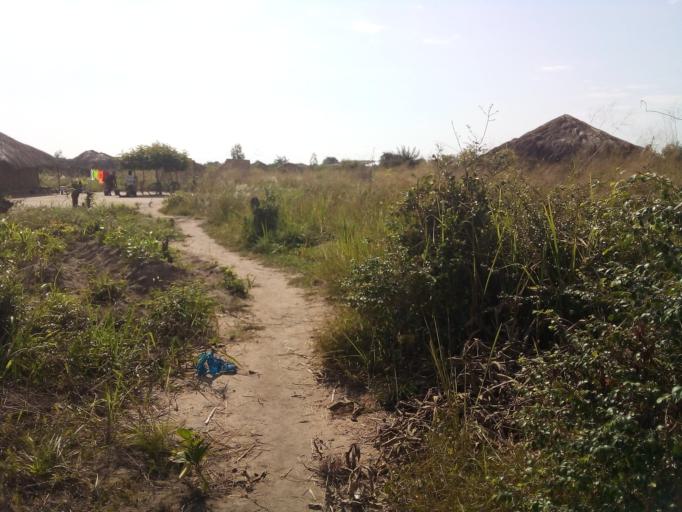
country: MZ
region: Zambezia
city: Quelimane
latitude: -17.5528
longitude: 36.7068
